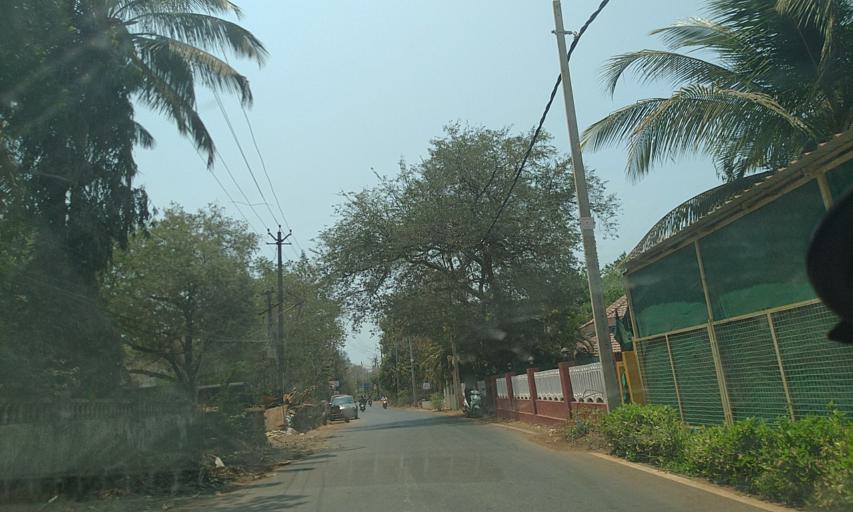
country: IN
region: Goa
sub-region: North Goa
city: Solim
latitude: 15.5924
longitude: 73.7749
